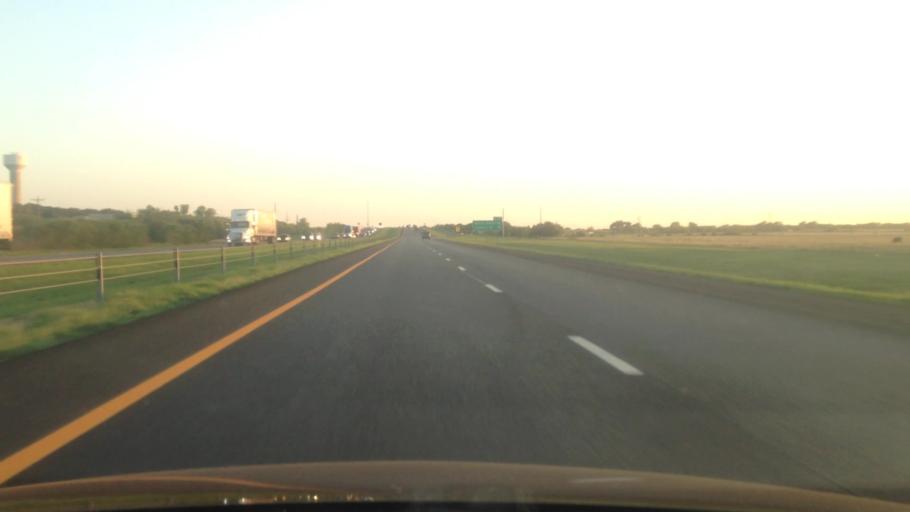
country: US
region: Texas
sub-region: Denton County
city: Argyle
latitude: 33.1369
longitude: -97.2034
